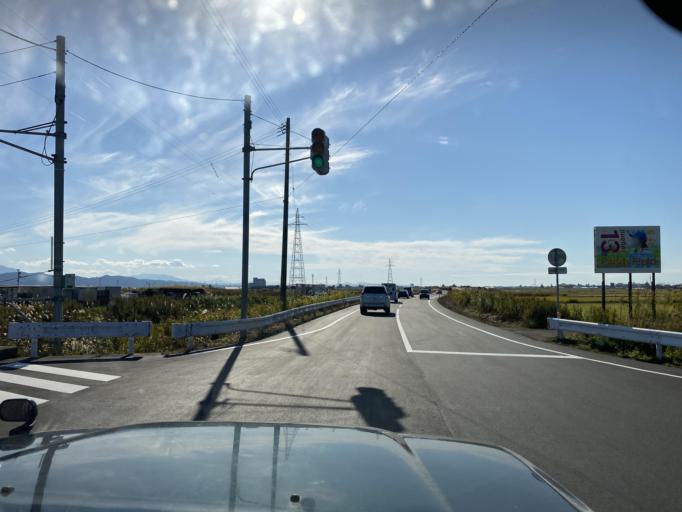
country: JP
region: Niigata
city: Niitsu-honcho
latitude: 37.8058
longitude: 139.0791
